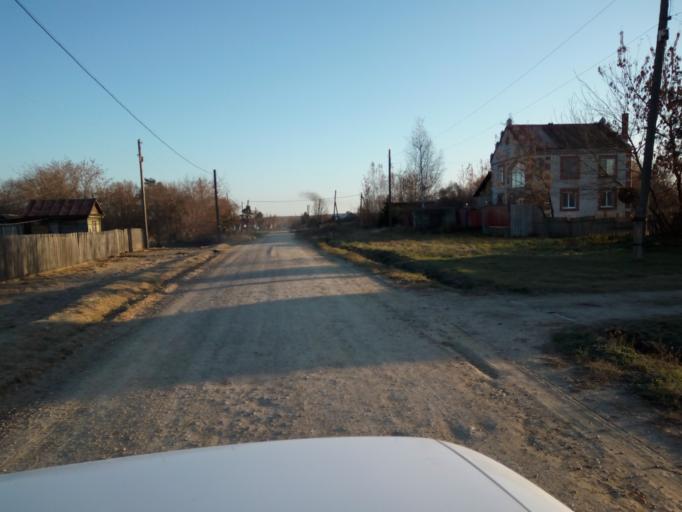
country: RU
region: Primorskiy
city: Lazo
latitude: 45.8780
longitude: 133.6515
